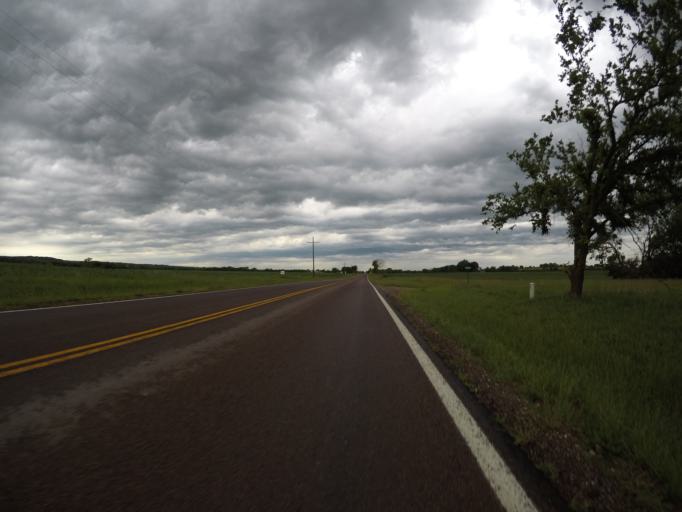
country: US
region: Kansas
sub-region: Shawnee County
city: Auburn
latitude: 38.9645
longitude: -95.9666
